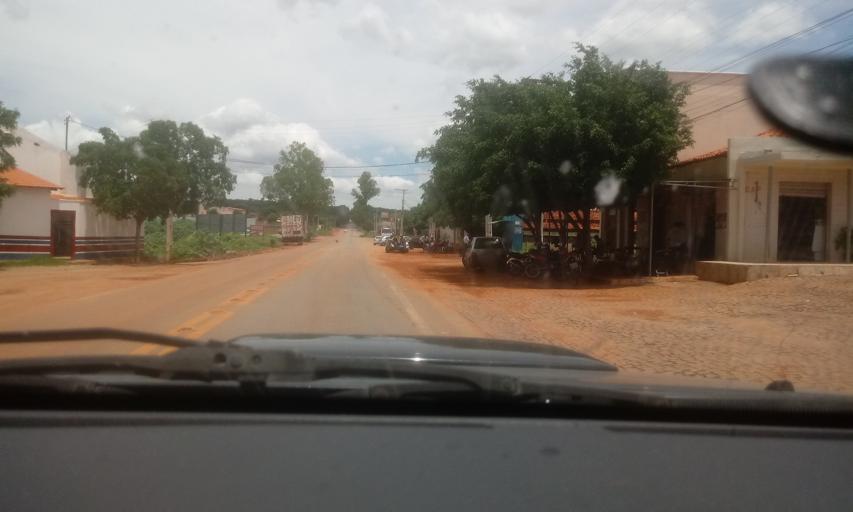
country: BR
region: Bahia
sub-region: Riacho De Santana
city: Riacho de Santana
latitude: -13.6042
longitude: -42.9385
